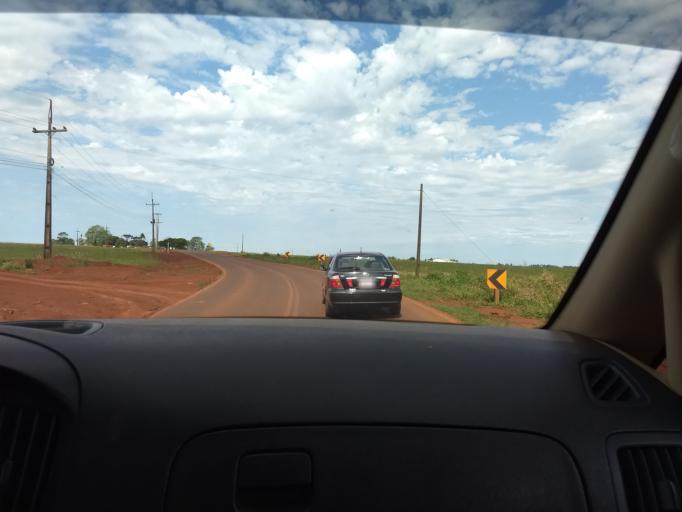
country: PY
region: Alto Parana
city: Santa Rita
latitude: -25.8020
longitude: -55.0673
